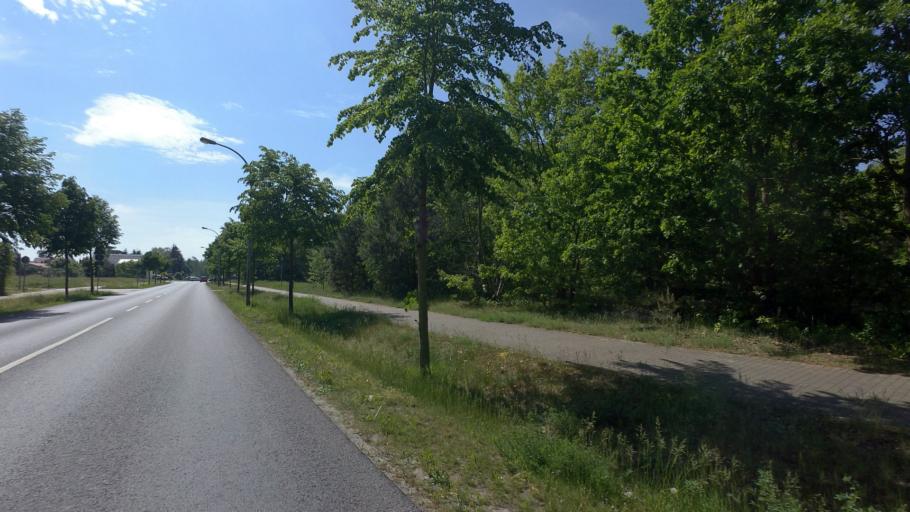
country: DE
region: Brandenburg
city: Oranienburg
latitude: 52.7283
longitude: 13.2397
